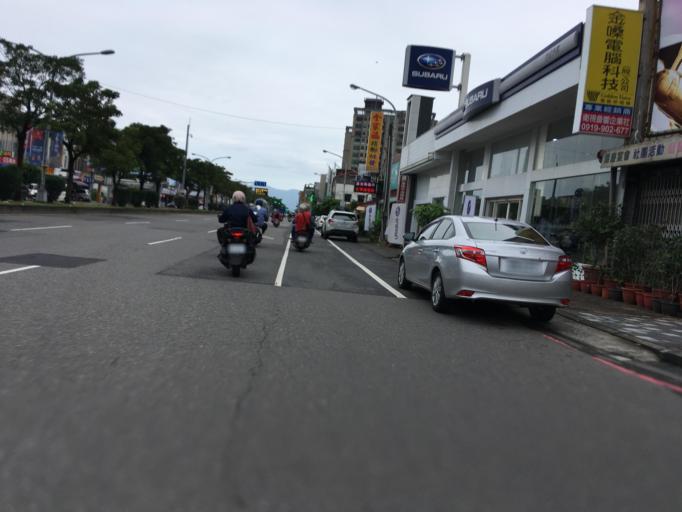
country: TW
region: Taiwan
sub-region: Yilan
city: Yilan
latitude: 24.6880
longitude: 121.7707
